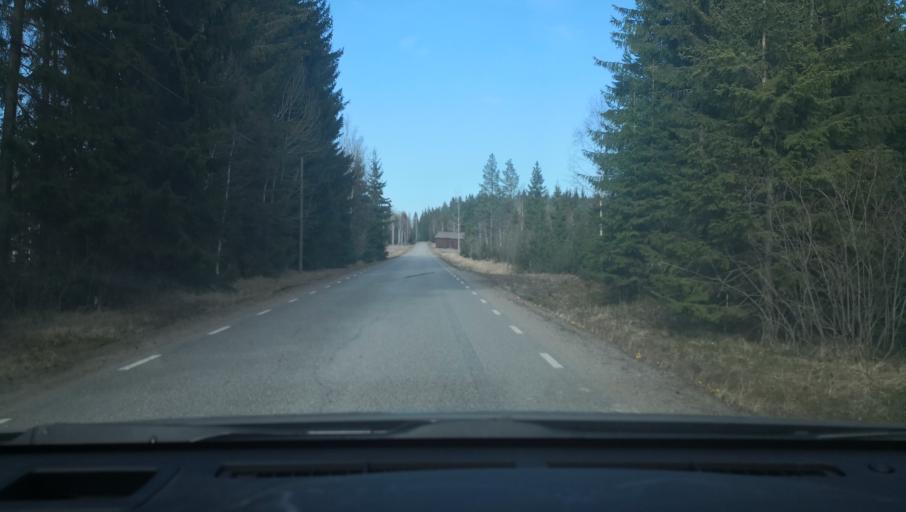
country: SE
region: Uppsala
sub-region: Heby Kommun
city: Heby
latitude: 59.9124
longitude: 16.8290
